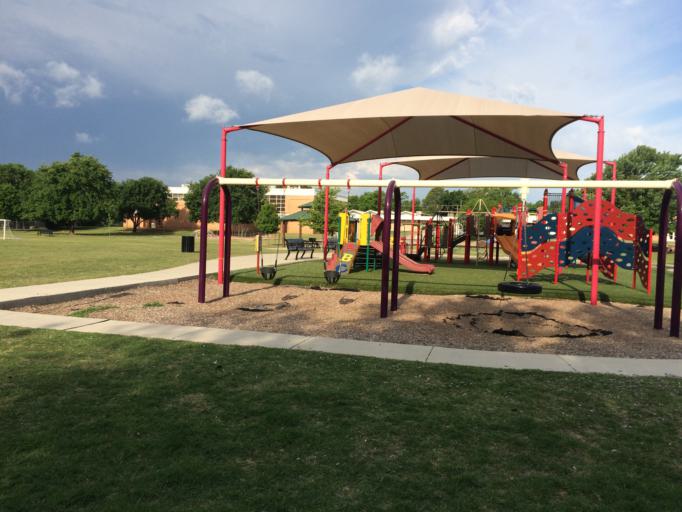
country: US
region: Oklahoma
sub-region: Cleveland County
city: Norman
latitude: 35.1986
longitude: -97.4655
